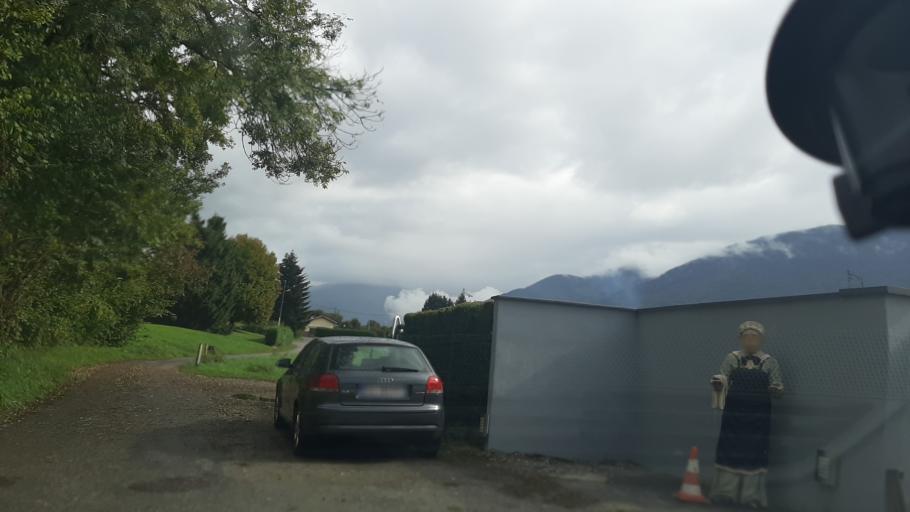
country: FR
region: Rhone-Alpes
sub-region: Departement de la Savoie
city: Frontenex
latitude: 45.6290
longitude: 6.3031
